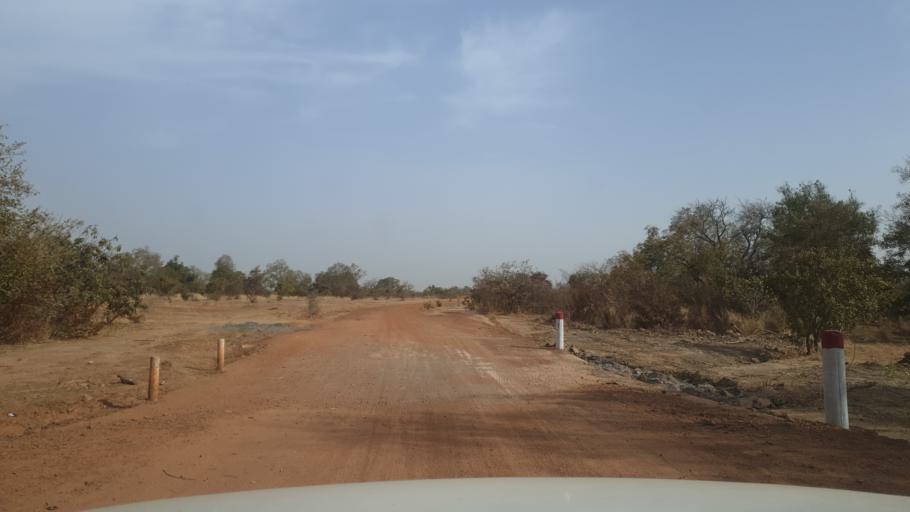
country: ML
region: Koulikoro
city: Kolokani
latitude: 13.3101
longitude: -8.2792
